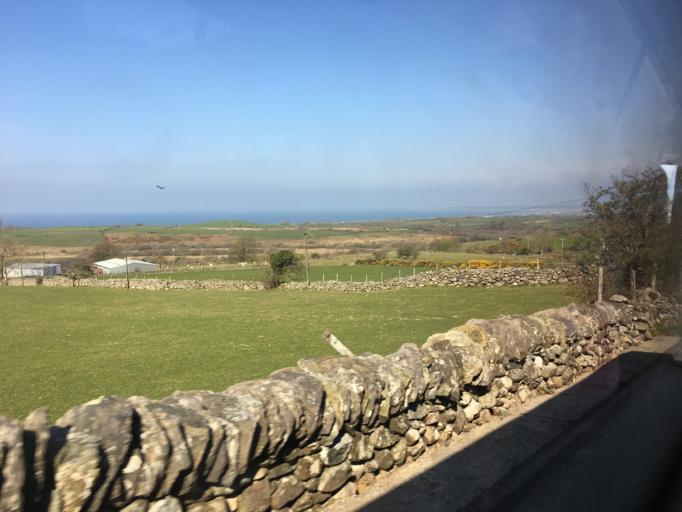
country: GB
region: Wales
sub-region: Gwynedd
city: Llanwnda
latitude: 53.0322
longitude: -4.2861
